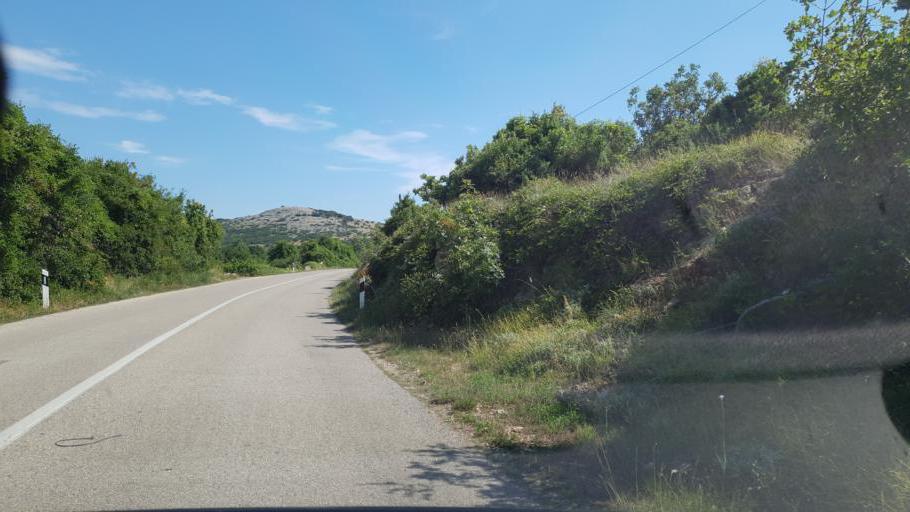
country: HR
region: Primorsko-Goranska
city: Punat
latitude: 44.9999
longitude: 14.6349
